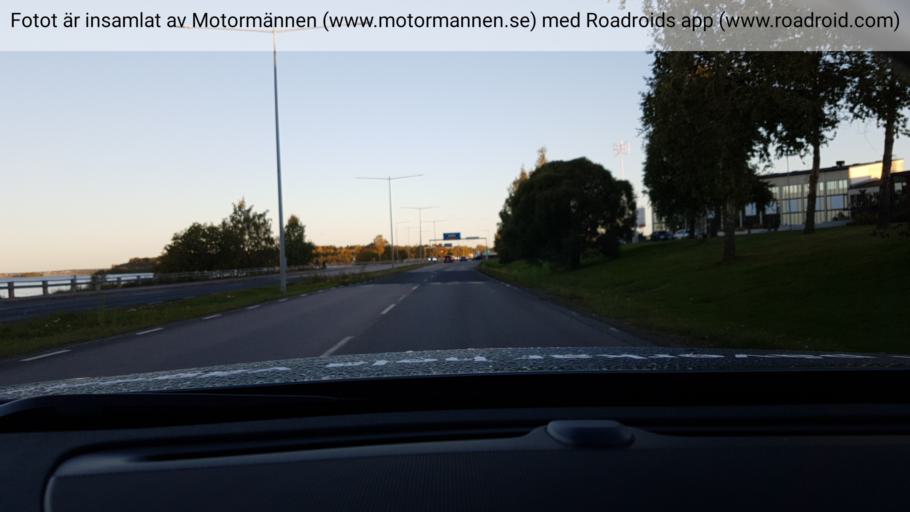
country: SE
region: Norrbotten
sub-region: Lulea Kommun
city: Lulea
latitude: 65.5873
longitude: 22.1494
